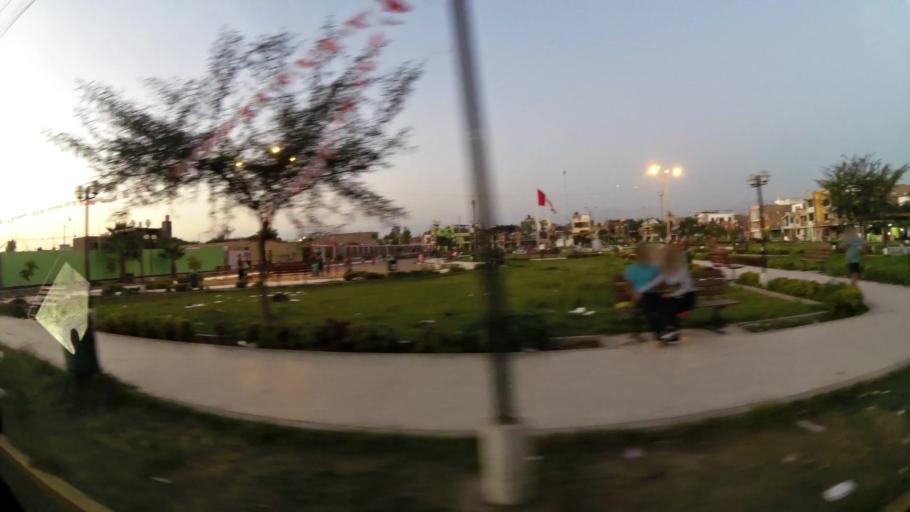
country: PE
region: Ica
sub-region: Provincia de Ica
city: Ica
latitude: -14.0818
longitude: -75.7329
